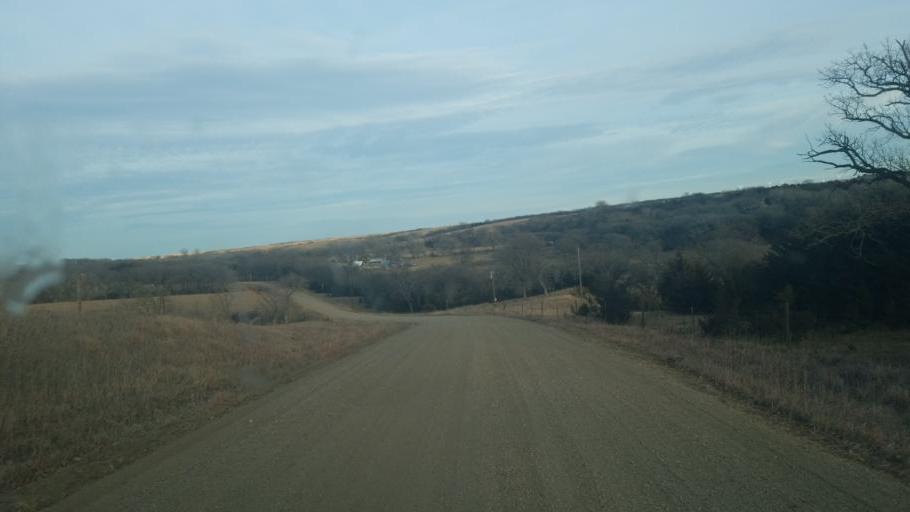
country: US
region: Nebraska
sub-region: Knox County
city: Center
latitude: 42.6919
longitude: -97.7988
